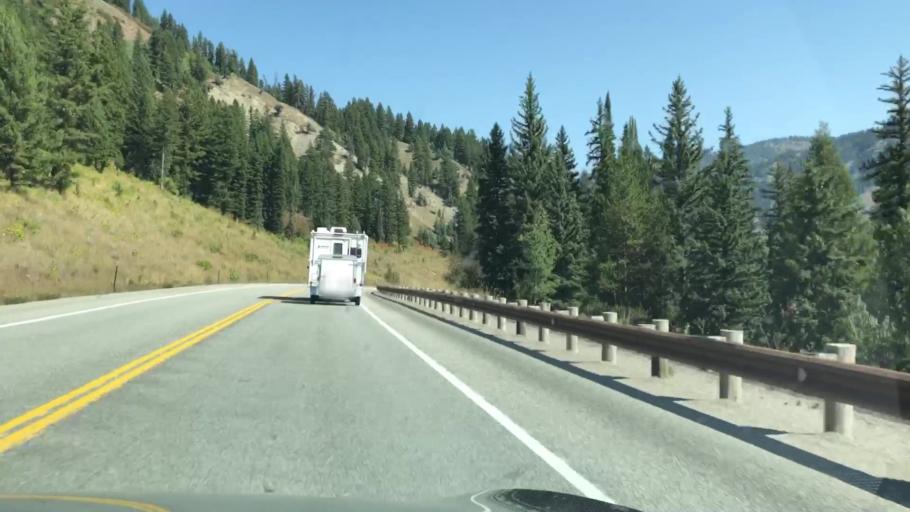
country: US
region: Wyoming
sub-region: Teton County
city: Hoback
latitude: 43.2270
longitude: -110.7850
